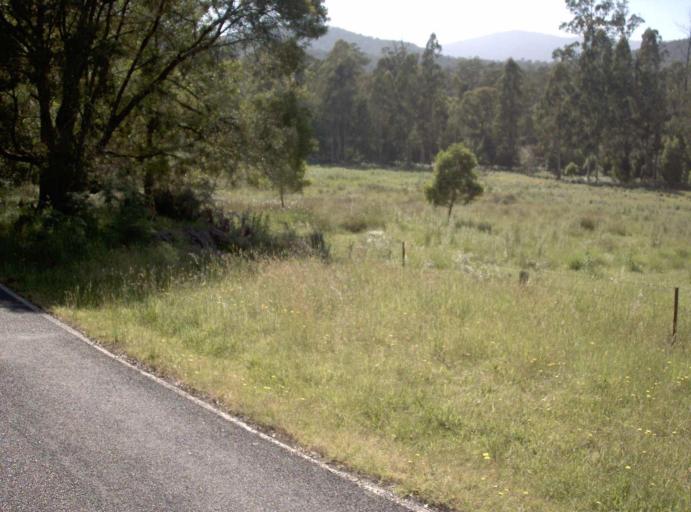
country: AU
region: New South Wales
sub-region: Bombala
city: Bombala
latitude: -37.3443
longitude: 148.6947
